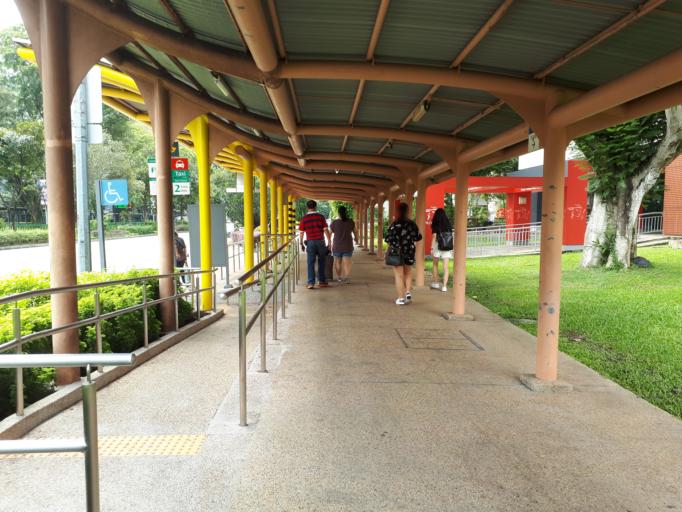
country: SG
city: Singapore
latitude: 1.3123
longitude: 103.8376
